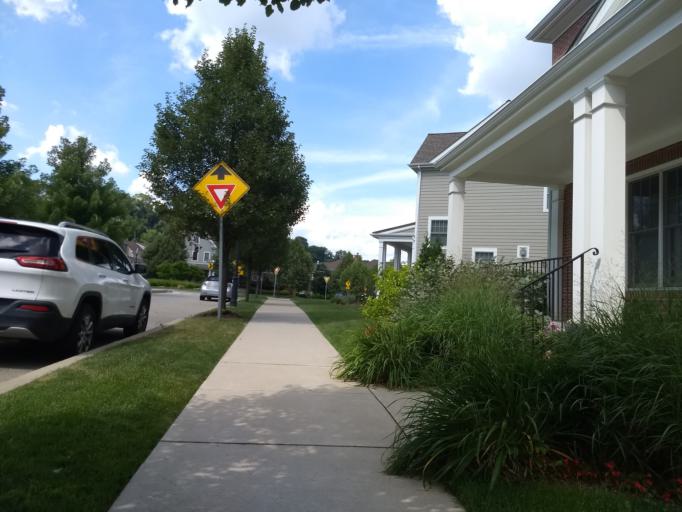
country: US
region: Pennsylvania
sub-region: Allegheny County
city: Homestead
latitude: 40.4163
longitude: -79.9206
